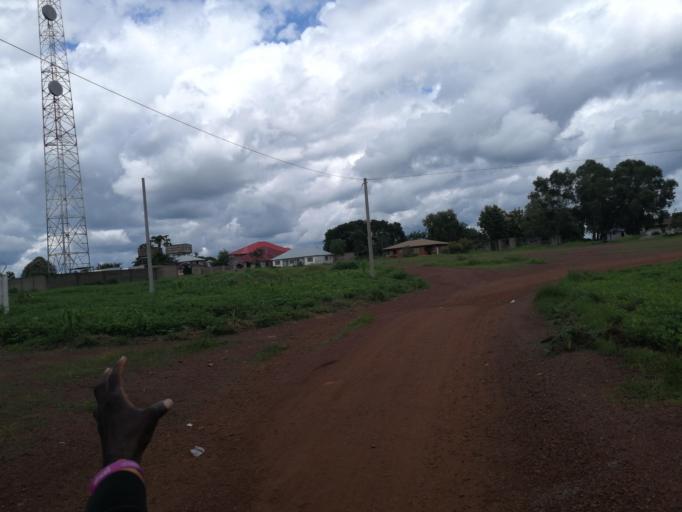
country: SL
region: Northern Province
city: Port Loko
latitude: 8.7681
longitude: -12.7804
